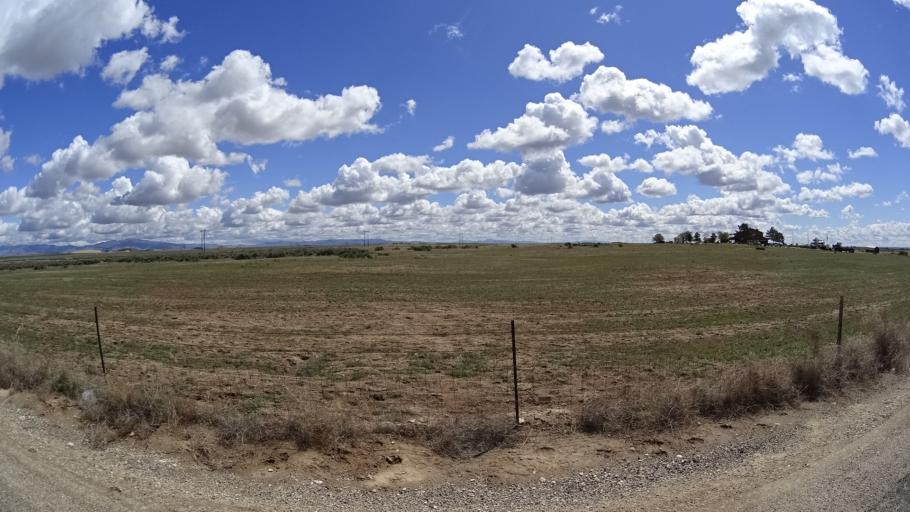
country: US
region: Idaho
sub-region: Ada County
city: Kuna
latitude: 43.4720
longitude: -116.2743
